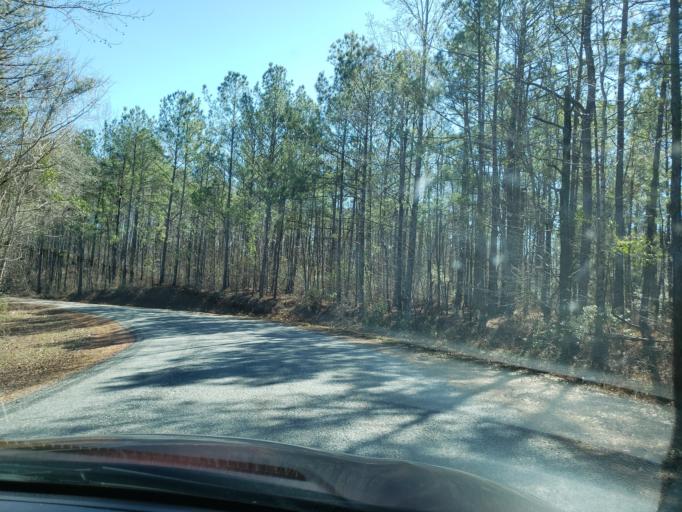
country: US
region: Alabama
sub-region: Elmore County
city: Tallassee
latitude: 32.6628
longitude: -85.8697
